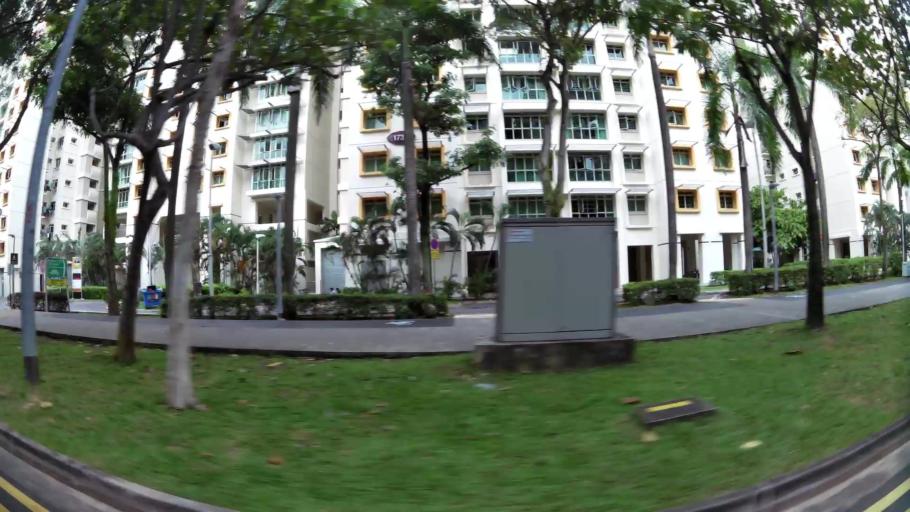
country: MY
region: Johor
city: Kampung Pasir Gudang Baru
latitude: 1.3961
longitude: 103.9103
